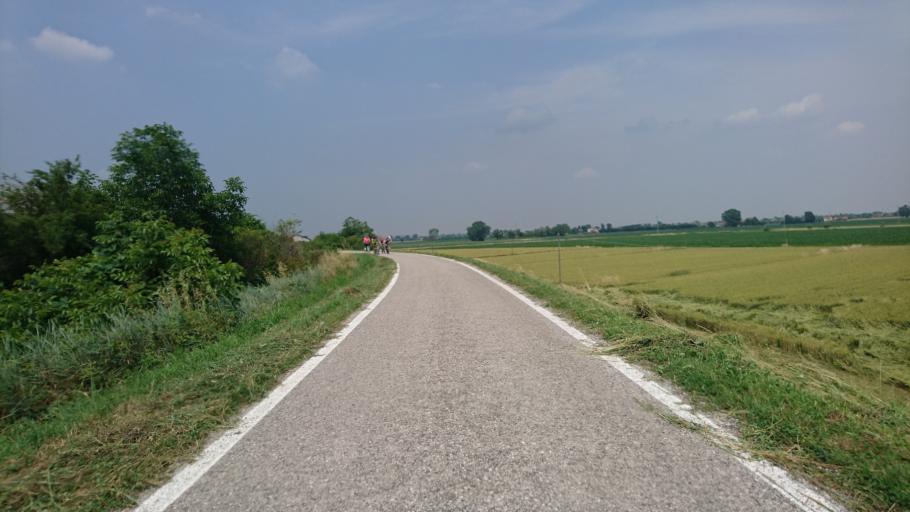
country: IT
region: Veneto
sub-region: Provincia di Padova
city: Bovolenta
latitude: 45.2720
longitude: 11.9274
